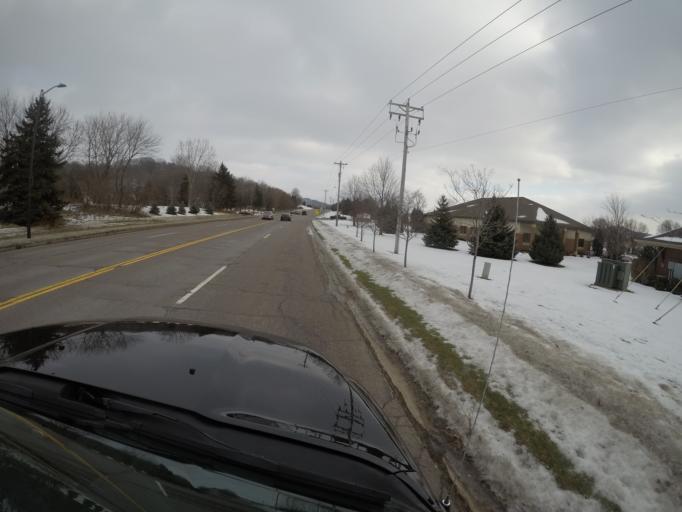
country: US
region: Wisconsin
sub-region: La Crosse County
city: Onalaska
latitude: 43.8810
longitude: -91.1891
